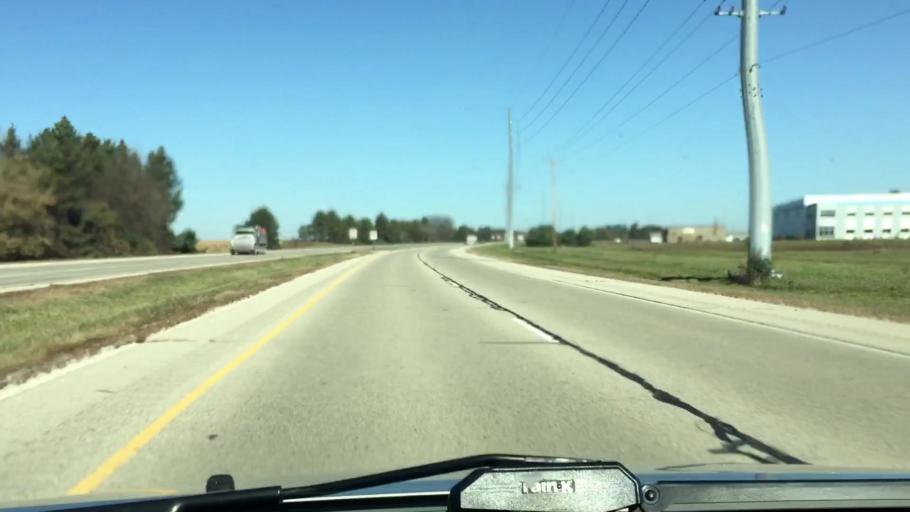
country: US
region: Wisconsin
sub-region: Waukesha County
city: Sussex
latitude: 43.1051
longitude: -88.2097
